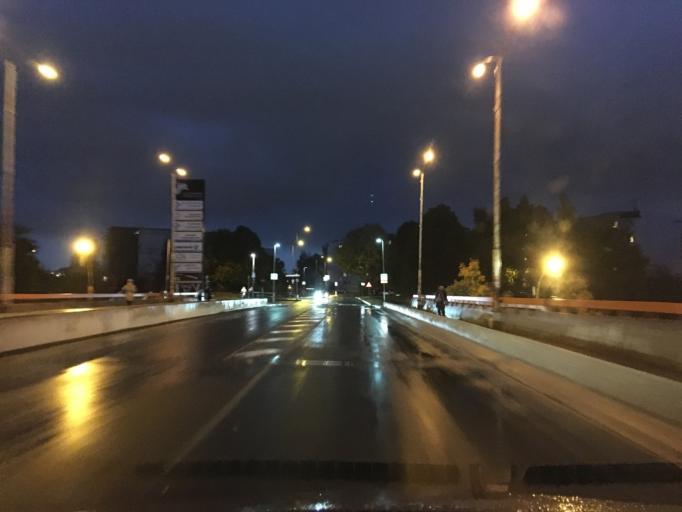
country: EE
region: Harju
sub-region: Tallinna linn
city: Tallinn
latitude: 59.4351
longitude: 24.7984
